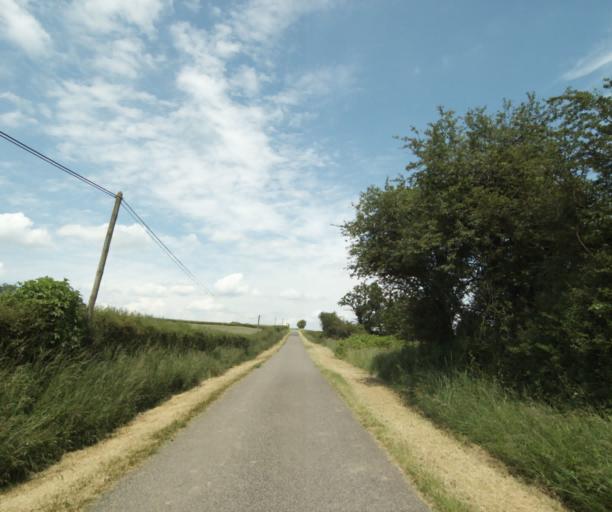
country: FR
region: Bourgogne
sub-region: Departement de Saone-et-Loire
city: Perrecy-les-Forges
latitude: 46.5906
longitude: 4.1410
